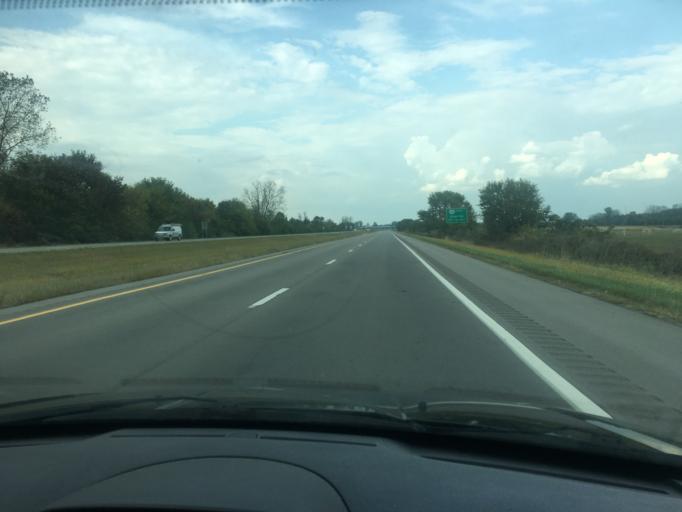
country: US
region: Ohio
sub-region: Clark County
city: Northridge
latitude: 39.9757
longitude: -83.8159
